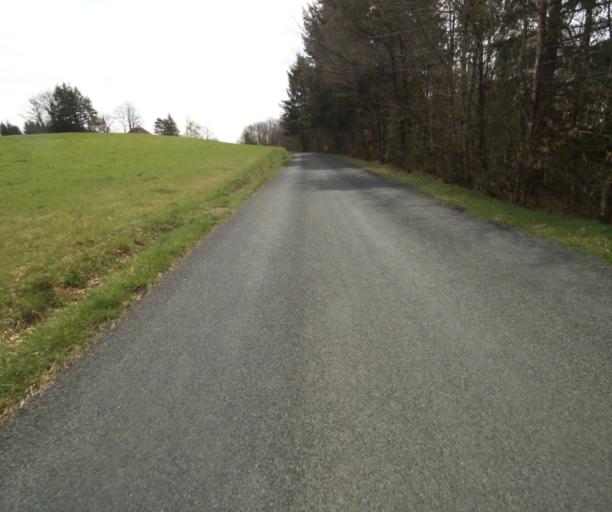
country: FR
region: Limousin
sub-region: Departement de la Correze
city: Sainte-Fortunade
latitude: 45.1995
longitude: 1.8351
